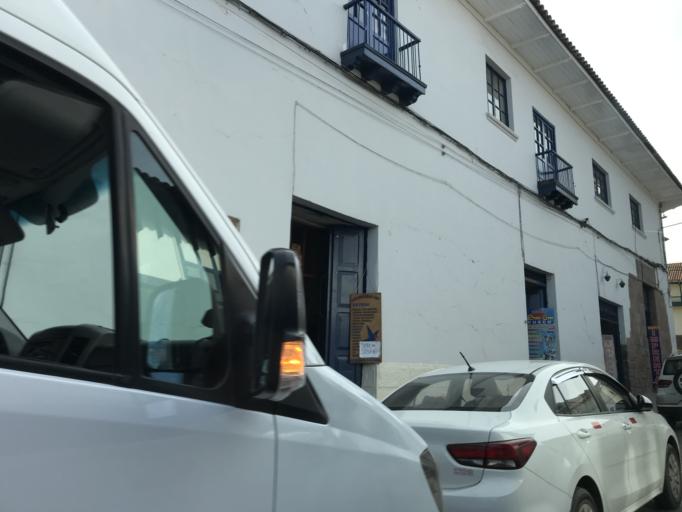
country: PE
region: Cusco
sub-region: Provincia de Cusco
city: Cusco
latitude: -13.5159
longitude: -71.9811
